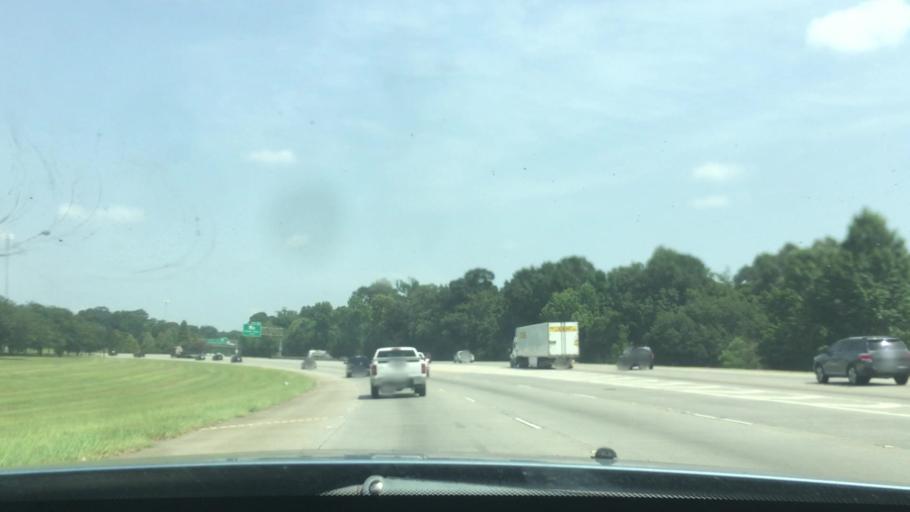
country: US
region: Louisiana
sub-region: East Baton Rouge Parish
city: Westminster
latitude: 30.4191
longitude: -91.1203
